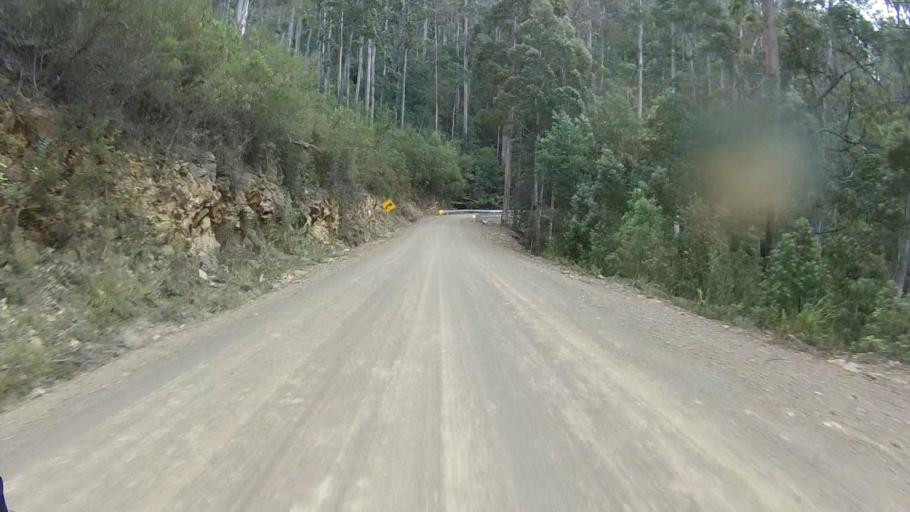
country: AU
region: Tasmania
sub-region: Sorell
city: Sorell
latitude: -42.6964
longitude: 147.8577
